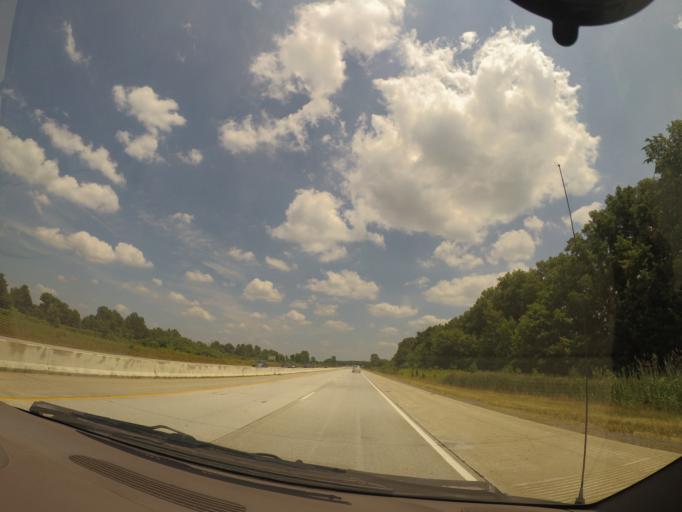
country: US
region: Indiana
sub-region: Saint Joseph County
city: Osceola
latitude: 41.6161
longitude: -86.0637
